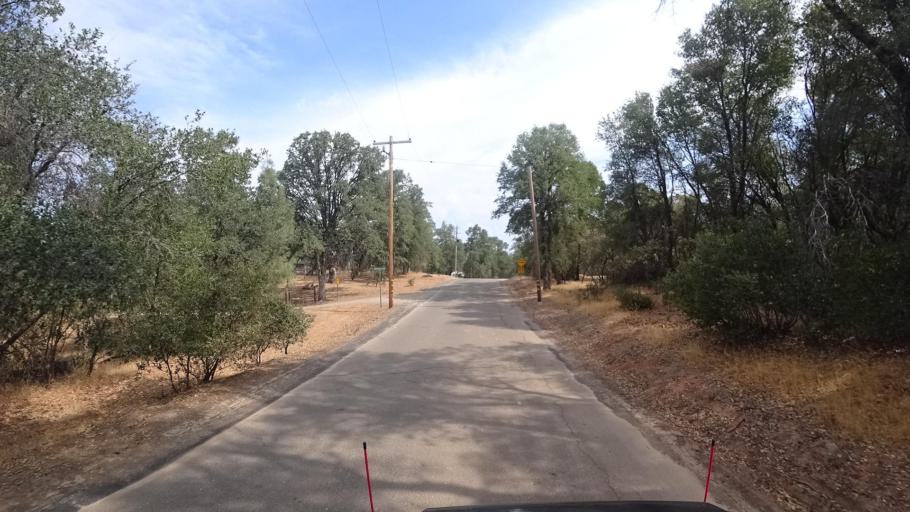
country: US
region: California
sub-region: Mariposa County
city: Midpines
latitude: 37.5669
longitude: -119.9693
